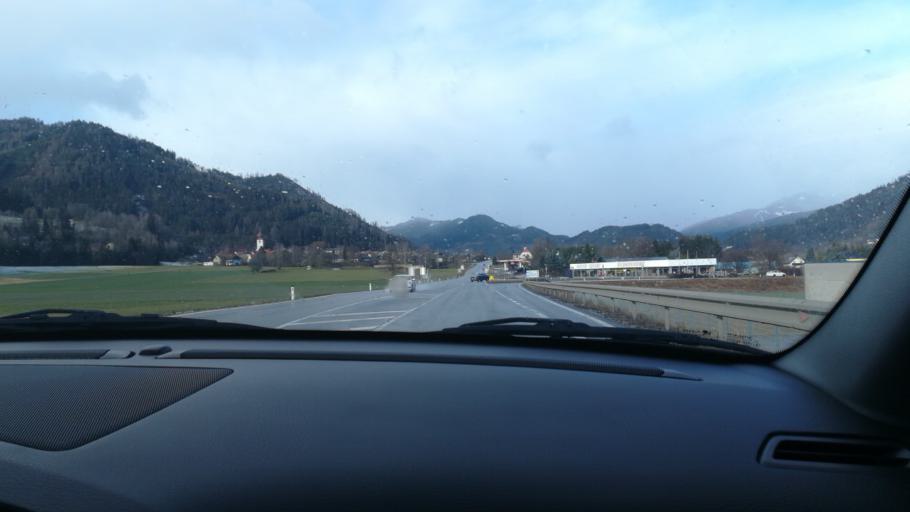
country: AT
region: Styria
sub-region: Politischer Bezirk Murtal
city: Sankt Peter ob Judenburg
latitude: 47.1820
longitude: 14.5995
